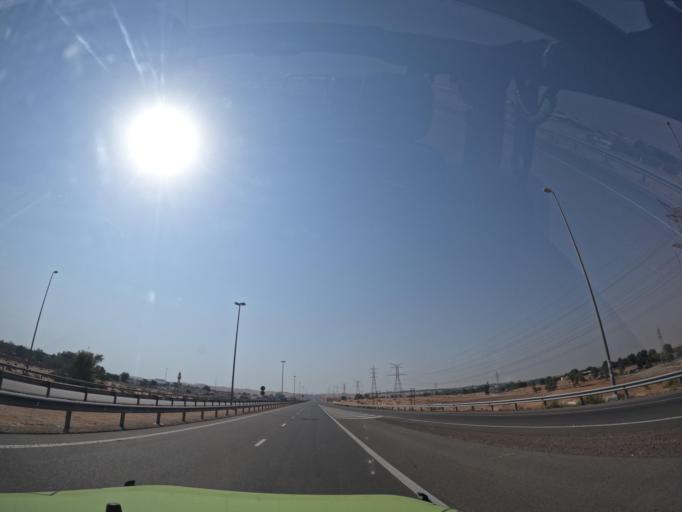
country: OM
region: Al Buraimi
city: Al Buraymi
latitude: 24.3641
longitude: 55.7298
